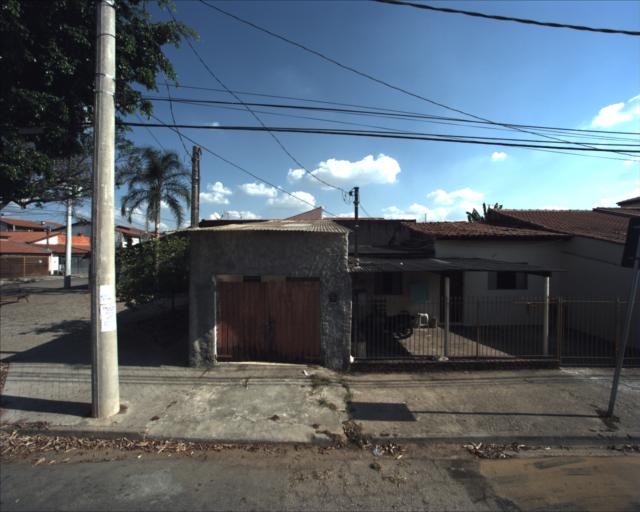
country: BR
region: Sao Paulo
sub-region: Sorocaba
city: Sorocaba
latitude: -23.4730
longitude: -47.4495
